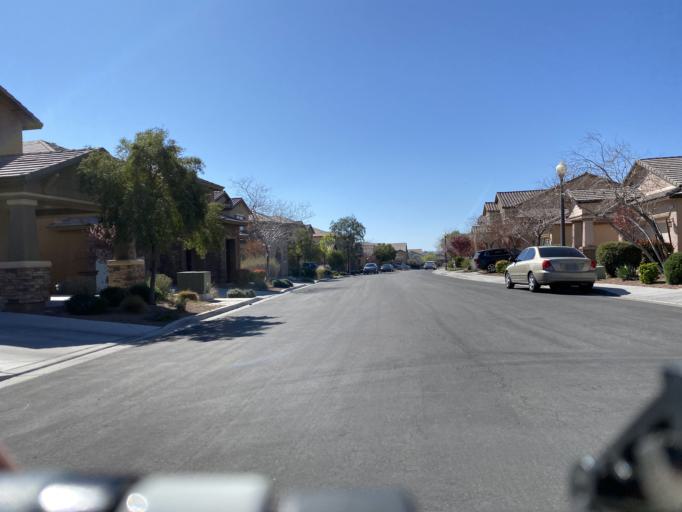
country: US
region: Nevada
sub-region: Clark County
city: Summerlin South
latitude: 36.2908
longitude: -115.3226
